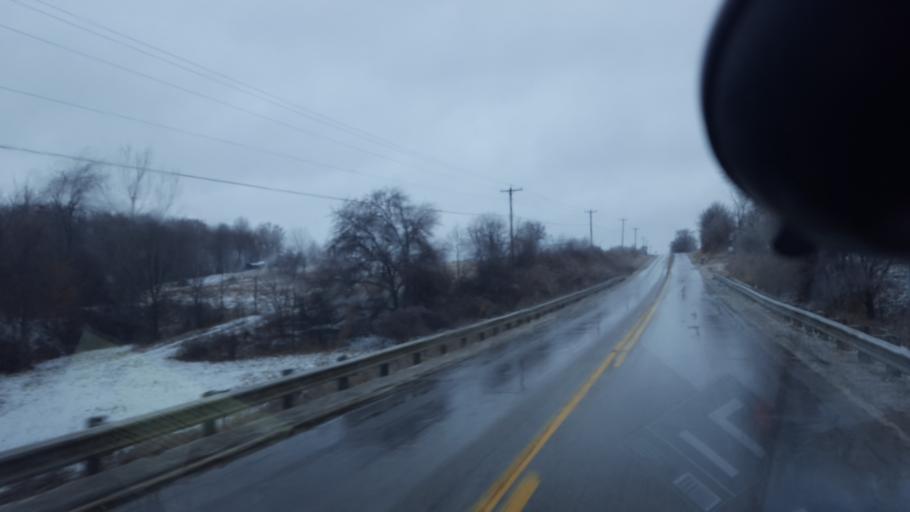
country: US
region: Ohio
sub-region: Richland County
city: Lexington
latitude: 40.6056
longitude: -82.6624
